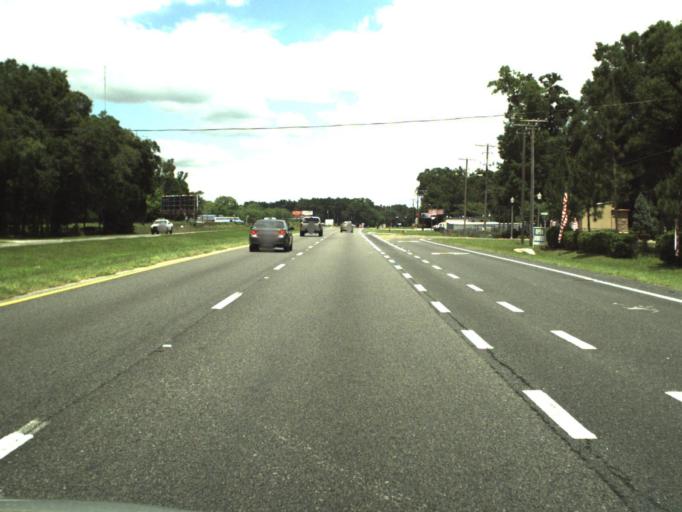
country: US
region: Florida
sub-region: Marion County
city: Ocala
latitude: 29.2330
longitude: -82.1504
